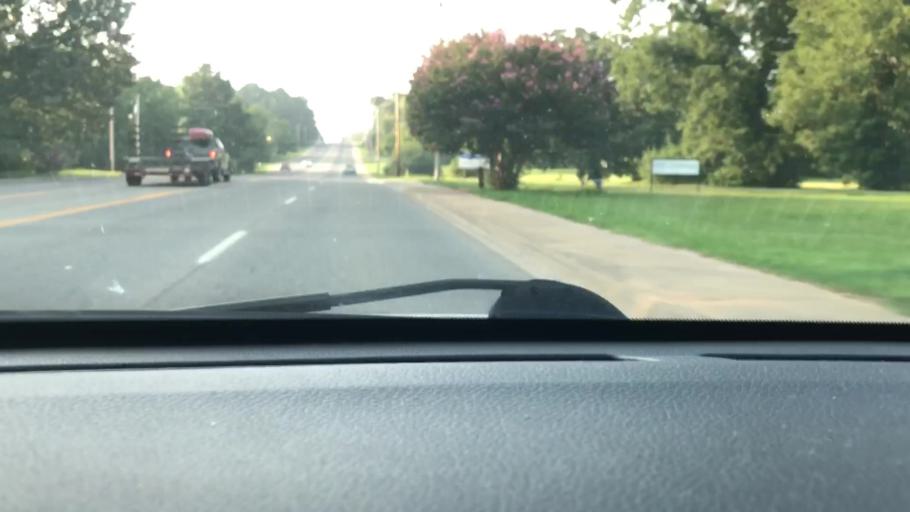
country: US
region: Arkansas
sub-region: Saline County
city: Bryant
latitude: 34.6076
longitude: -92.4923
